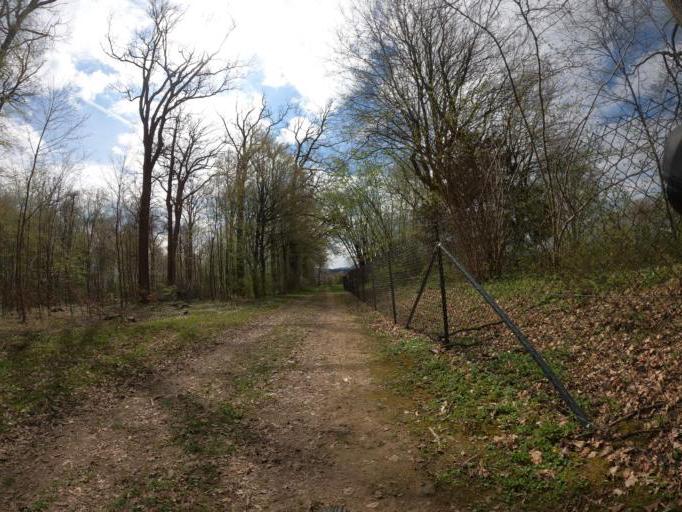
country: DE
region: Baden-Wuerttemberg
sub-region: Tuebingen Region
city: Wannweil
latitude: 48.5023
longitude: 9.1376
